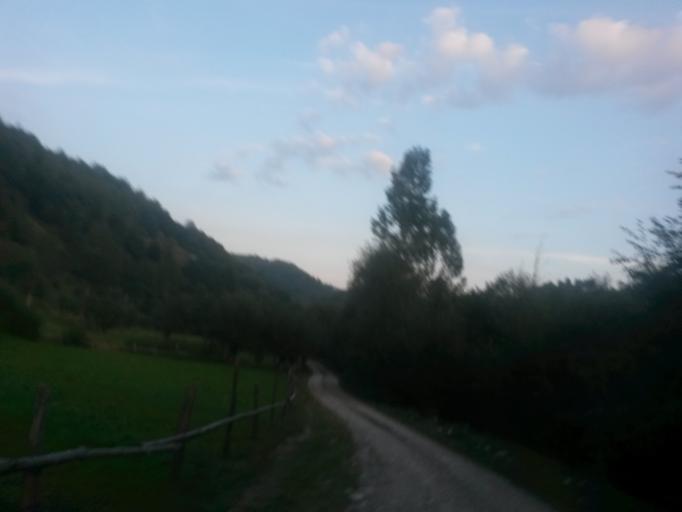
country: RO
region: Alba
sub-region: Comuna Ponor
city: Ponor
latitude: 46.3110
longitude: 23.4060
